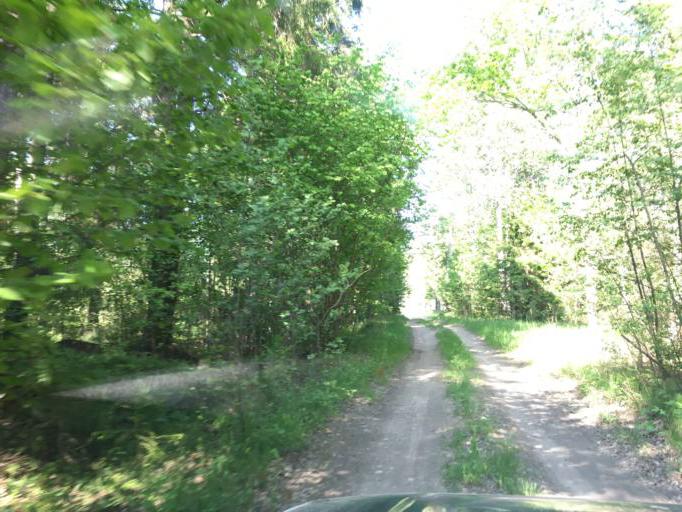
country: LV
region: Dundaga
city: Dundaga
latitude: 57.6038
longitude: 22.5094
